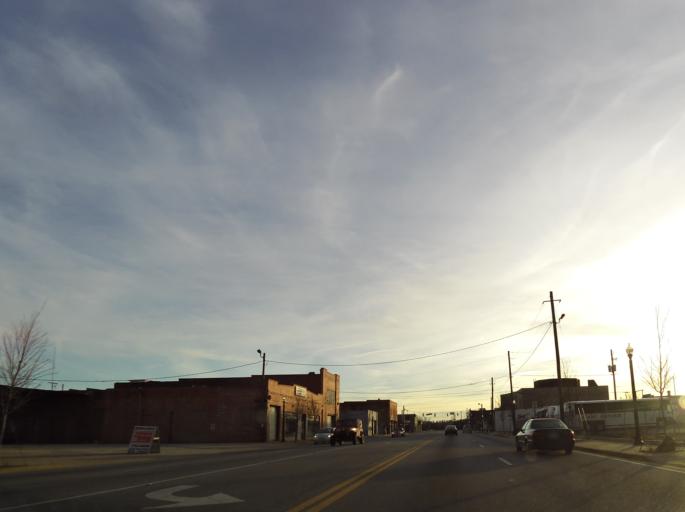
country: US
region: Georgia
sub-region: Bibb County
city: Macon
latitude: 32.8308
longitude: -83.6294
